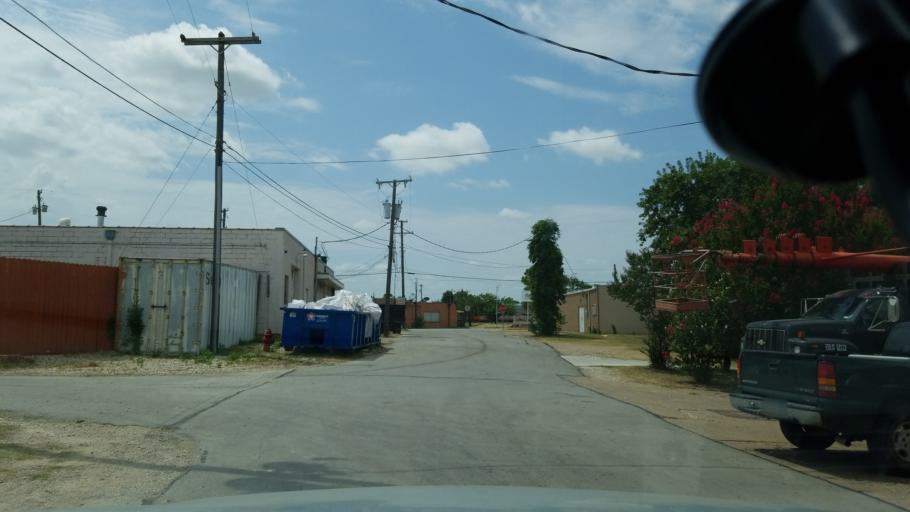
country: US
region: Texas
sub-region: Dallas County
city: Grand Prairie
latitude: 32.7470
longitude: -96.9966
